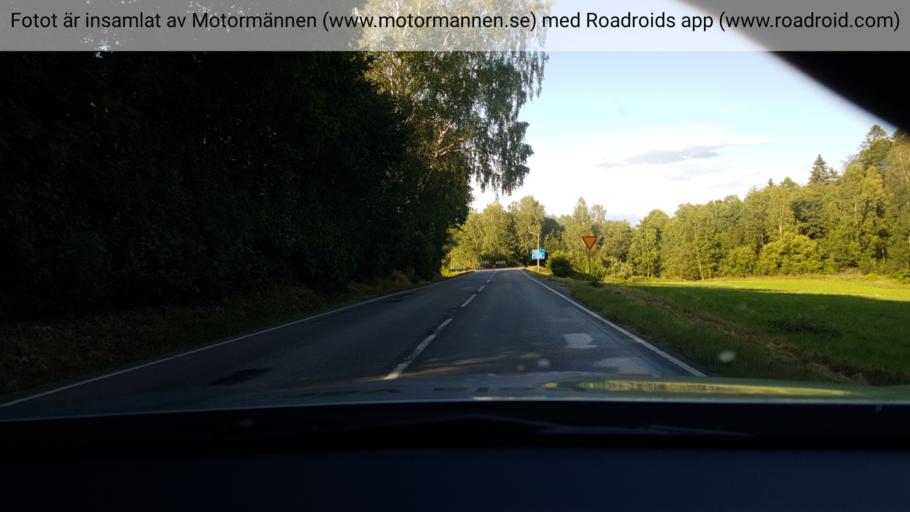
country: SE
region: Vaestra Goetaland
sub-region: Harryda Kommun
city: Landvetter
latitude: 57.6808
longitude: 12.1815
